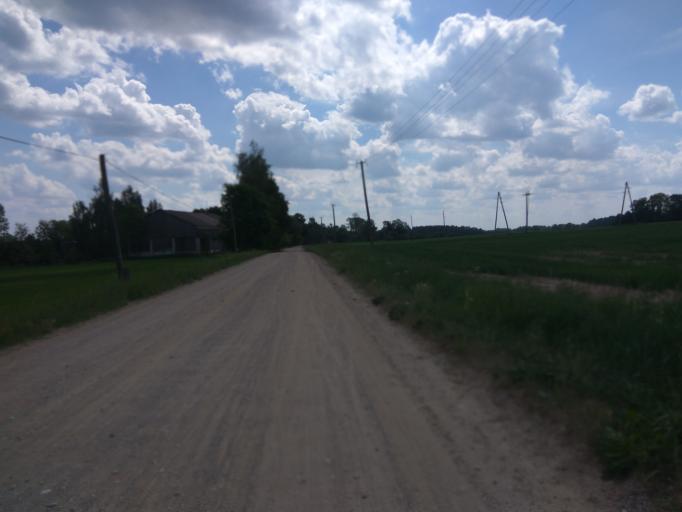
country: LV
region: Kuldigas Rajons
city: Kuldiga
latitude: 56.8946
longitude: 21.9694
